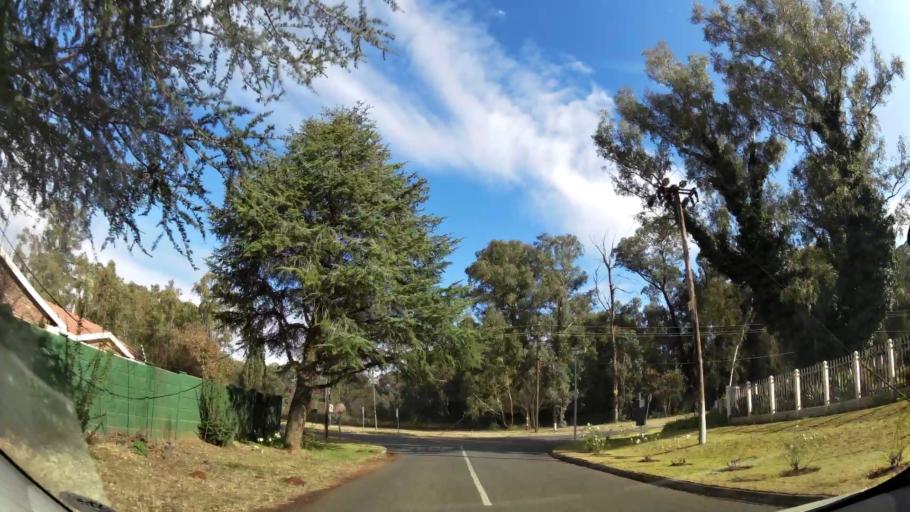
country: ZA
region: Gauteng
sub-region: Sedibeng District Municipality
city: Meyerton
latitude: -26.5478
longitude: 28.0613
